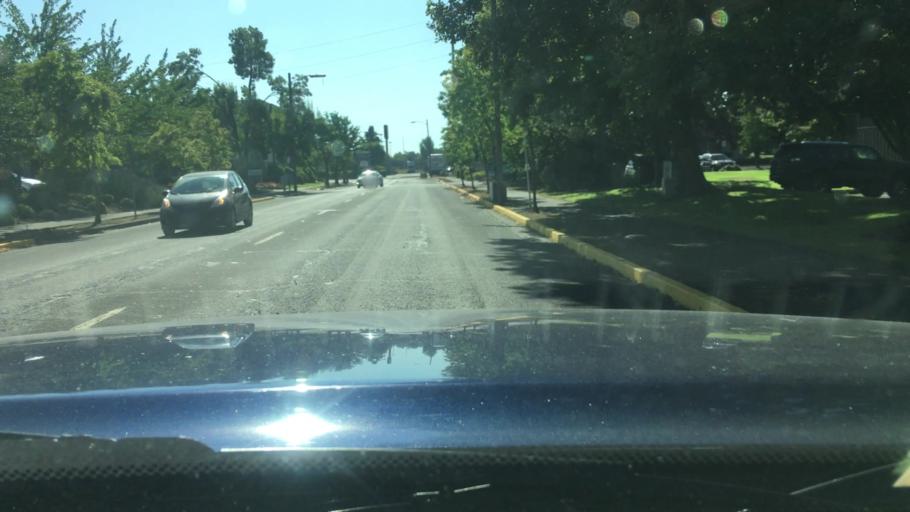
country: US
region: Oregon
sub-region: Lane County
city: Springfield
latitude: 44.0800
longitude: -123.0430
